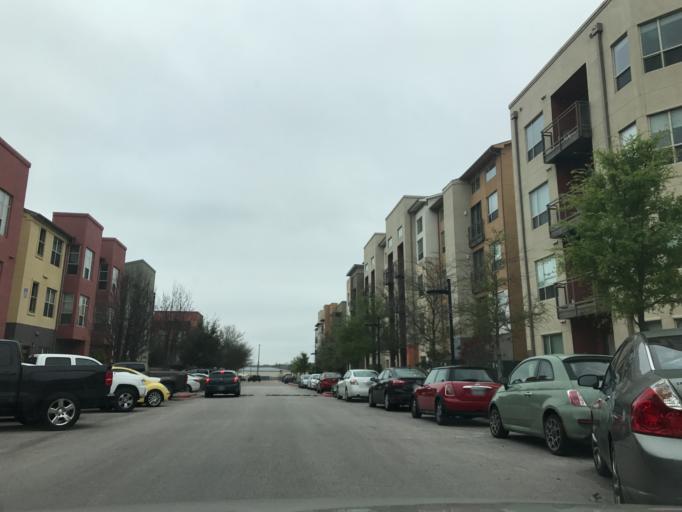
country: US
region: Texas
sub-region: Travis County
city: Austin
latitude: 30.3408
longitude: -97.7189
